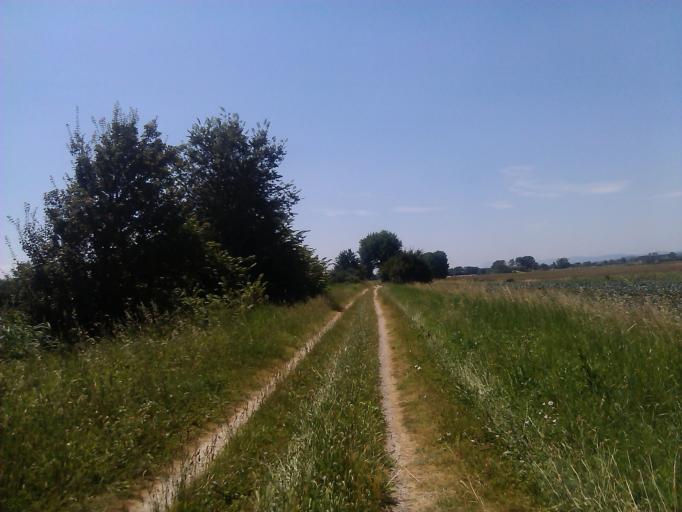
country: IT
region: Tuscany
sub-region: Province of Arezzo
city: Cesa
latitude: 43.3327
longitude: 11.8305
